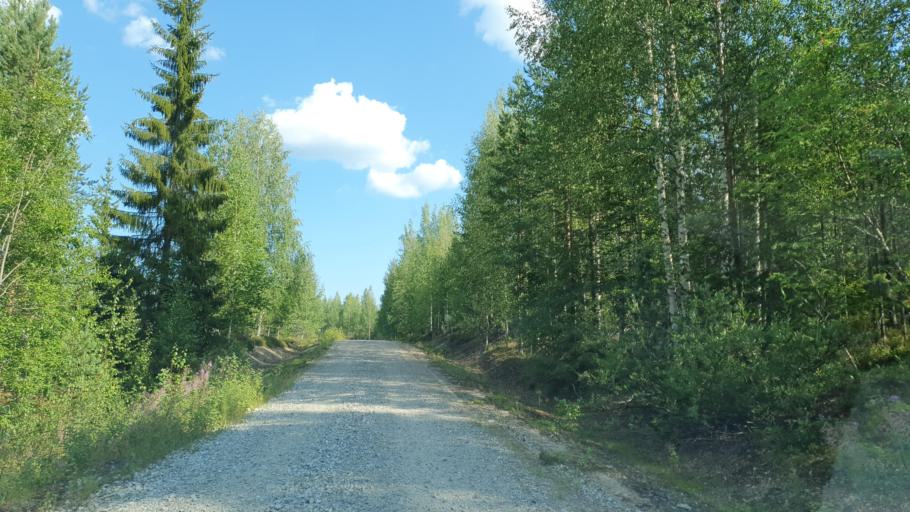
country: FI
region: Kainuu
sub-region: Kehys-Kainuu
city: Kuhmo
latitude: 63.9526
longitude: 29.5636
